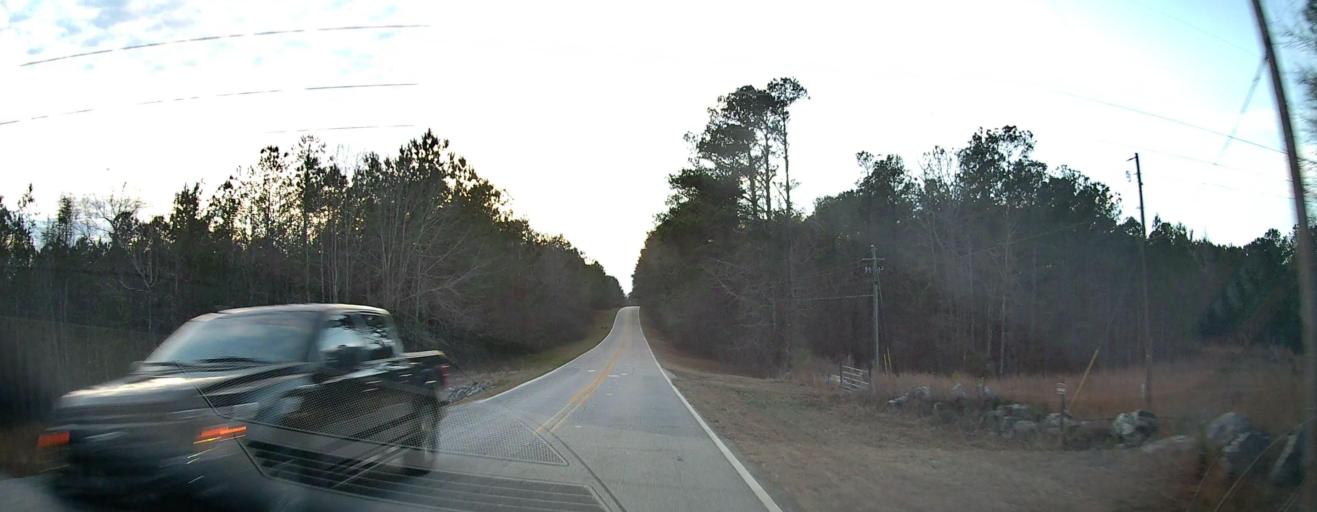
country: US
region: Alabama
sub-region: Russell County
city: Phenix City
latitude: 32.5970
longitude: -84.8982
